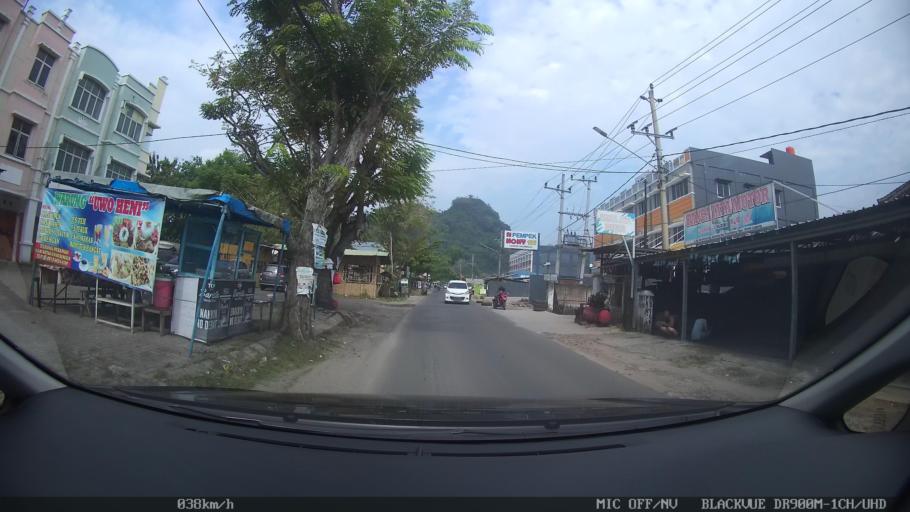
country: ID
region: Lampung
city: Bandarlampung
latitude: -5.4639
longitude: 105.2474
